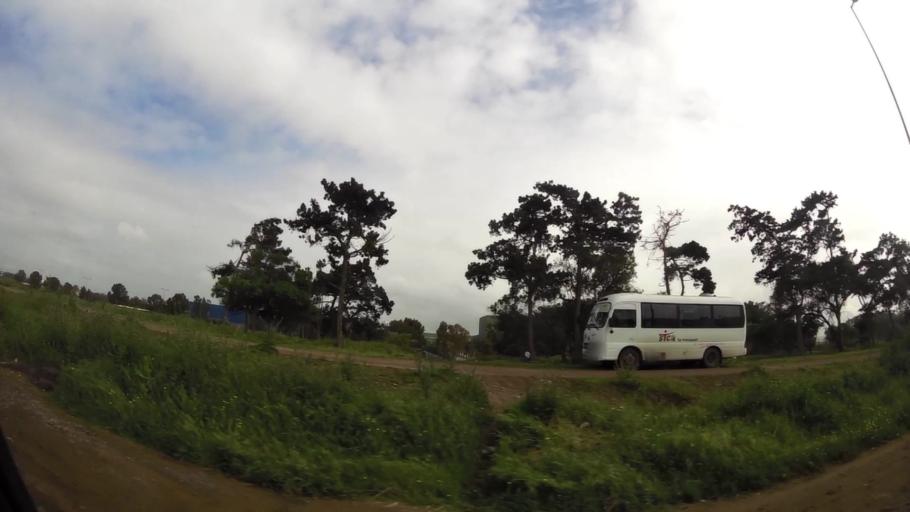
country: MA
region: Grand Casablanca
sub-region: Mohammedia
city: Mohammedia
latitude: 33.6405
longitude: -7.4378
